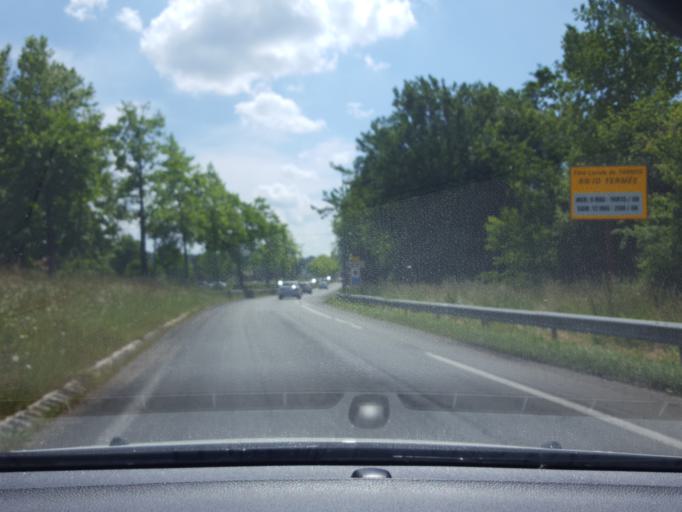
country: FR
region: Aquitaine
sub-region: Departement des Landes
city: Tarnos
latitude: 43.5546
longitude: -1.4564
